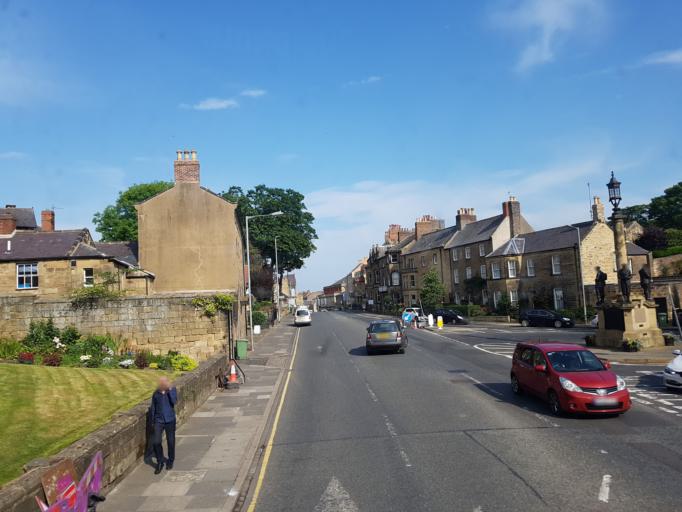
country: GB
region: England
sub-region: Northumberland
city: Alnwick
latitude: 55.4110
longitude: -1.7005
